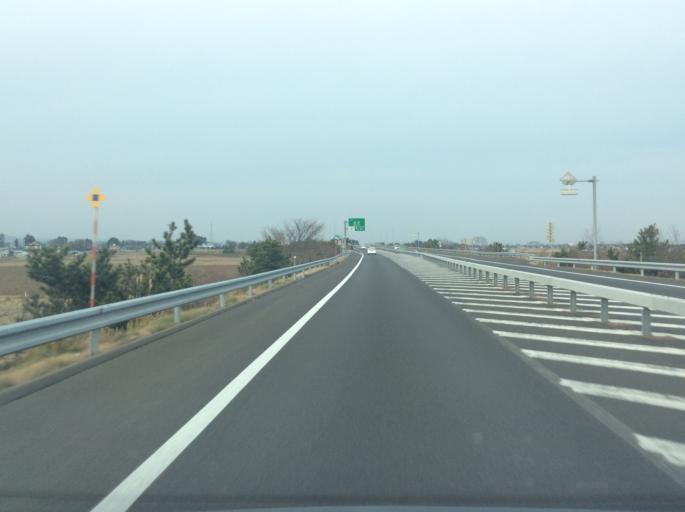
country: JP
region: Miyagi
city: Iwanuma
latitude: 38.1015
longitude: 140.8892
